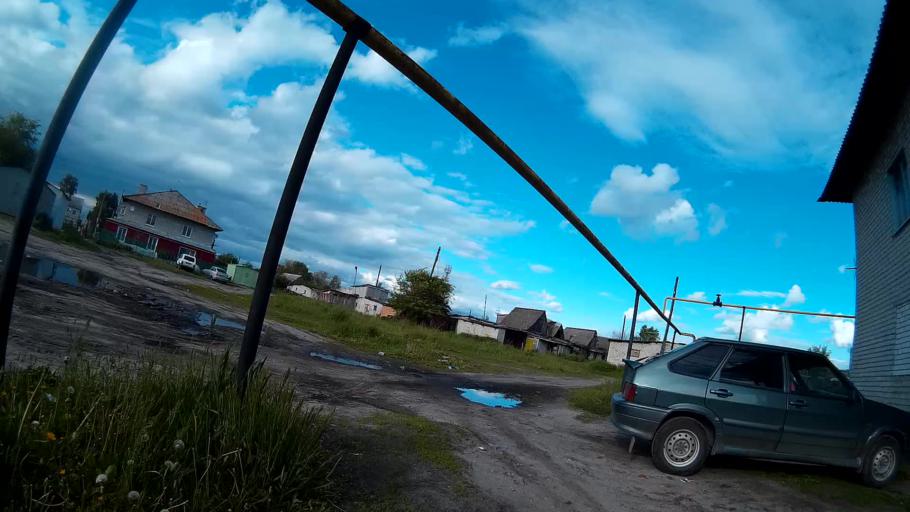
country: RU
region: Ulyanovsk
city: Novoul'yanovsk
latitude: 54.2034
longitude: 48.2675
